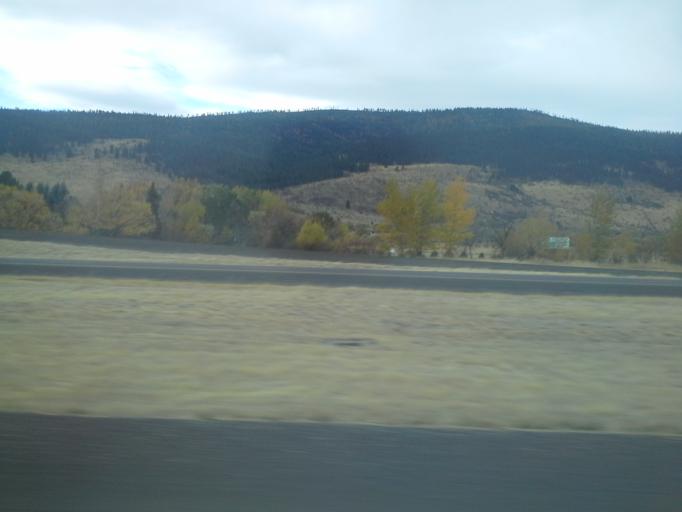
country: US
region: Oregon
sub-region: Union County
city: La Grande
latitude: 45.2499
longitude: -118.0197
